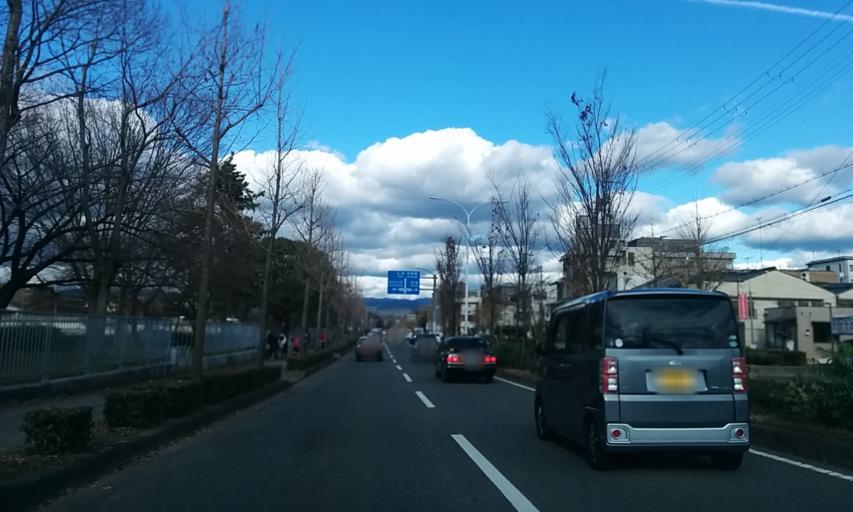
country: JP
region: Kyoto
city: Kyoto
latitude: 35.0160
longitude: 135.7722
